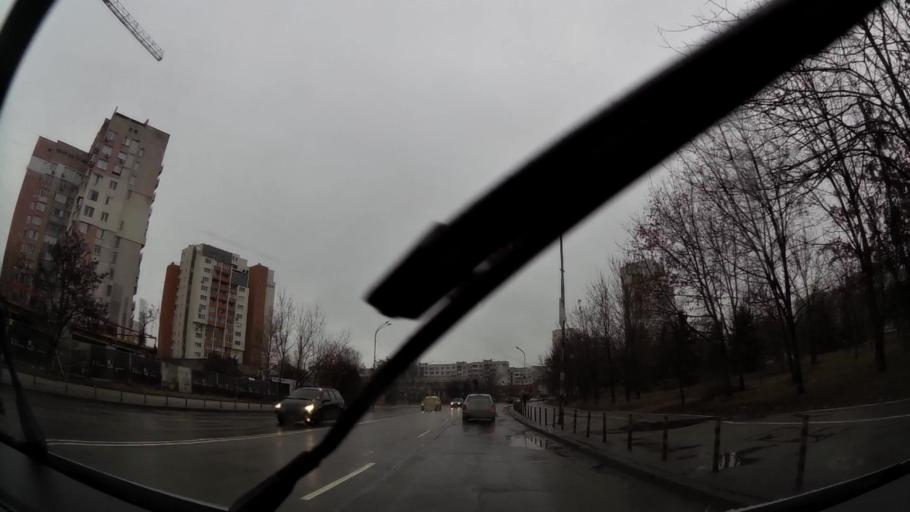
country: BG
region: Sofia-Capital
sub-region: Stolichna Obshtina
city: Sofia
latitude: 42.6420
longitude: 23.3809
